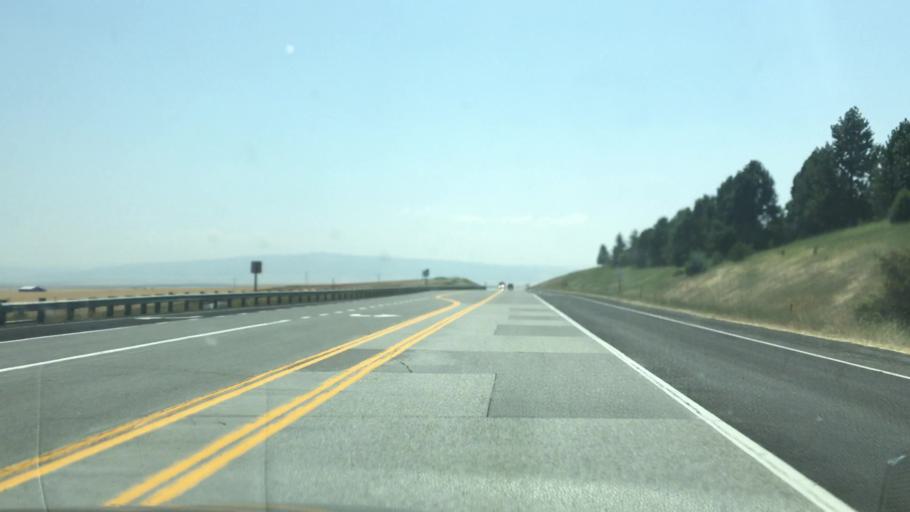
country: US
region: Idaho
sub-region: Lewis County
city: Nezperce
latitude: 46.0444
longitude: -116.3431
